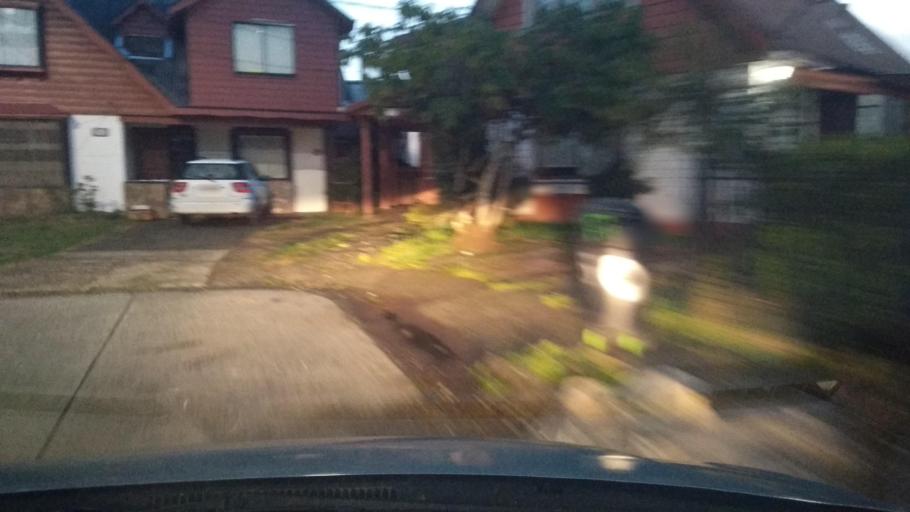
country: CL
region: Los Rios
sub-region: Provincia de Valdivia
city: Valdivia
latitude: -39.8109
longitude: -73.2615
